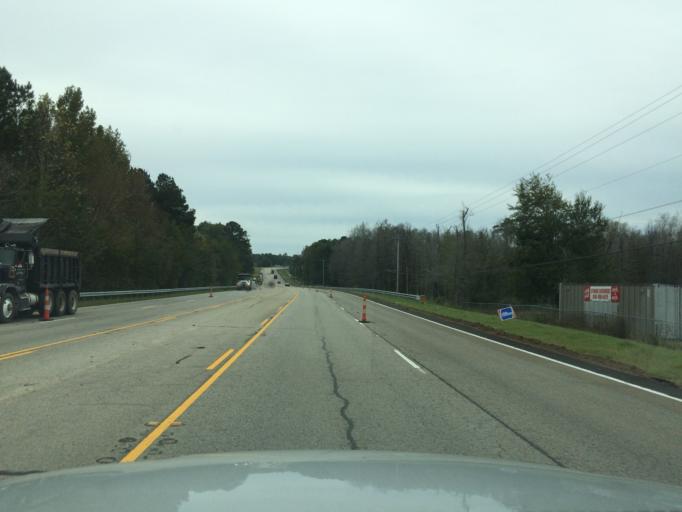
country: US
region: South Carolina
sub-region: Aiken County
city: Aiken
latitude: 33.6079
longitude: -81.6840
